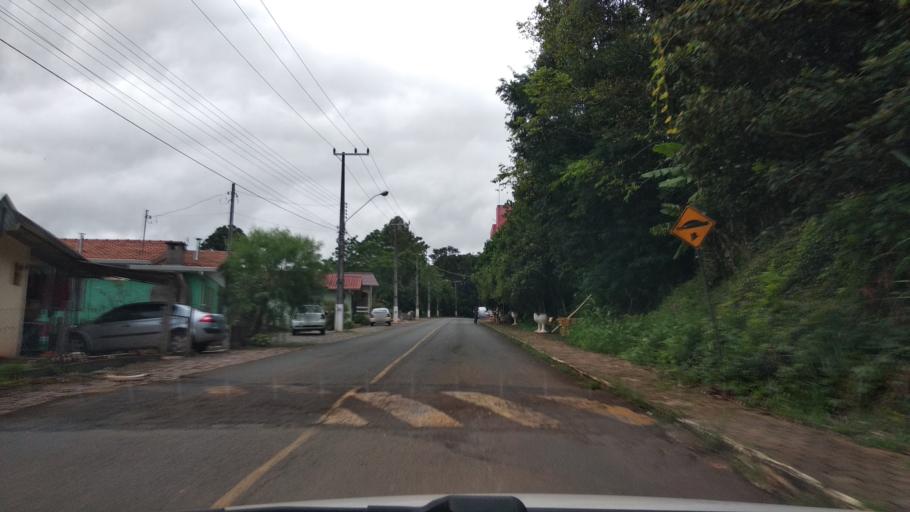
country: BR
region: Santa Catarina
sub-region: Videira
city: Videira
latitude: -27.0455
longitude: -51.2242
